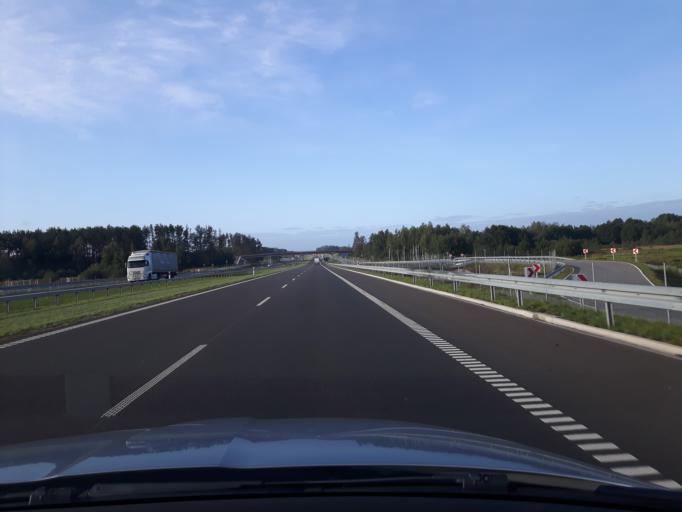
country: PL
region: Masovian Voivodeship
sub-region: Powiat radomski
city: Jedlinsk
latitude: 51.4916
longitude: 21.0722
